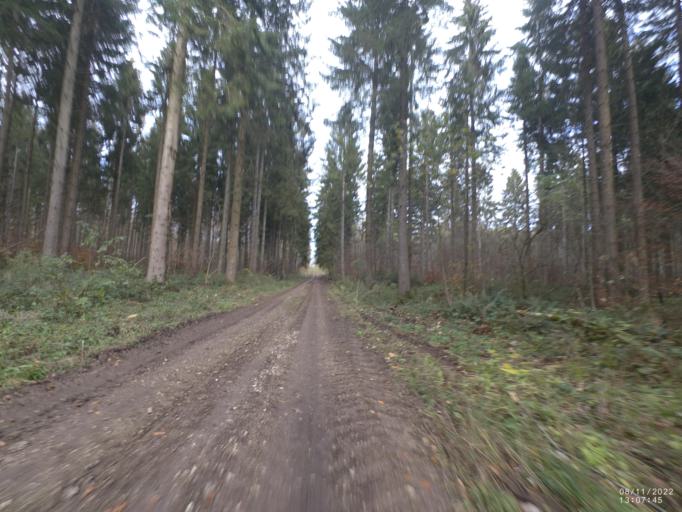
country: DE
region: Baden-Wuerttemberg
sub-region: Tuebingen Region
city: Nellingen
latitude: 48.5653
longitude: 9.7595
